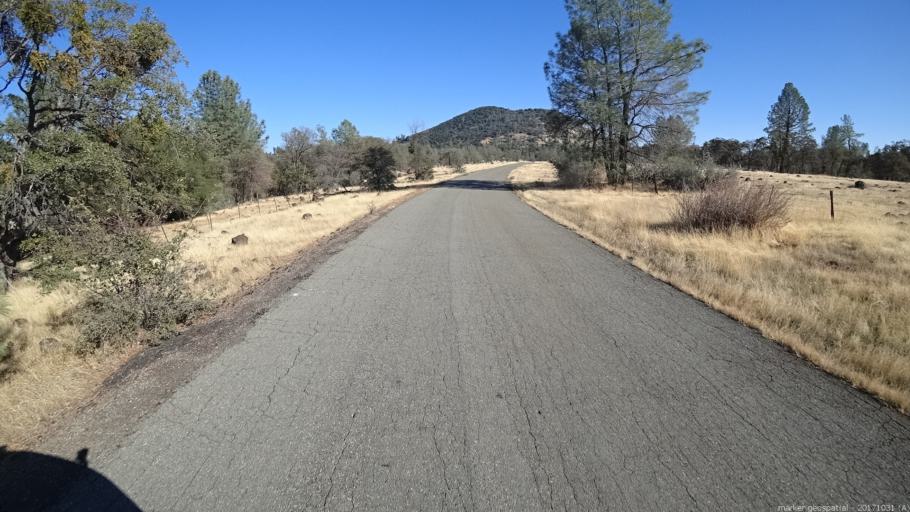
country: US
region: California
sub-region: Shasta County
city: Shingletown
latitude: 40.4583
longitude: -122.0196
